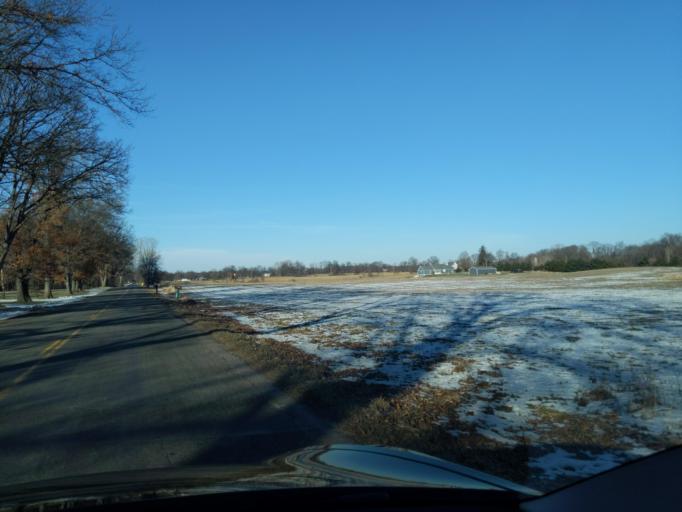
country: US
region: Michigan
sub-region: Ingham County
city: Stockbridge
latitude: 42.4424
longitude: -84.1506
